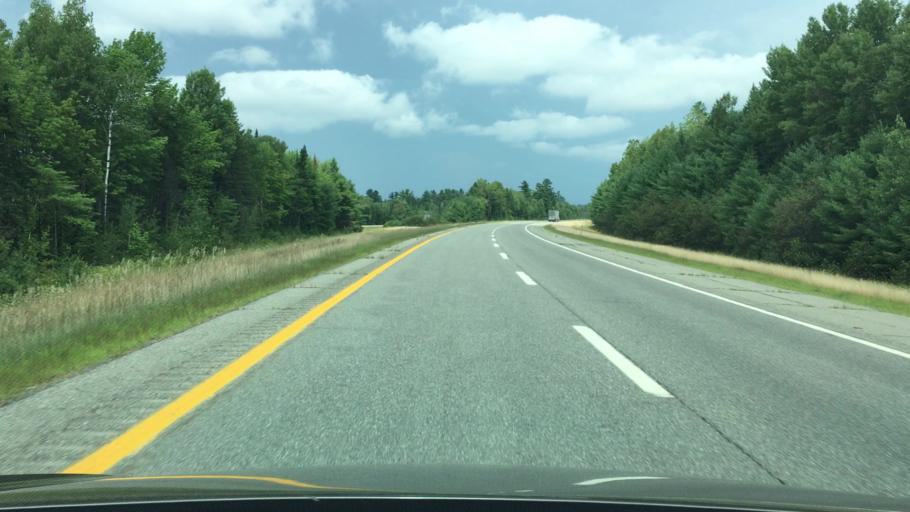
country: US
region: Maine
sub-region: Penobscot County
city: Lincoln
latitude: 45.3846
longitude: -68.6044
